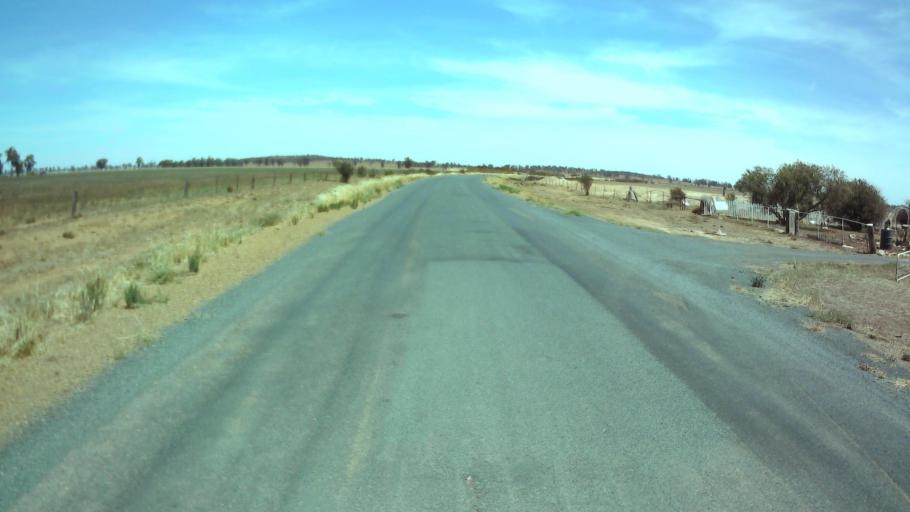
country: AU
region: New South Wales
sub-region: Weddin
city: Grenfell
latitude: -33.7501
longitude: 147.7670
